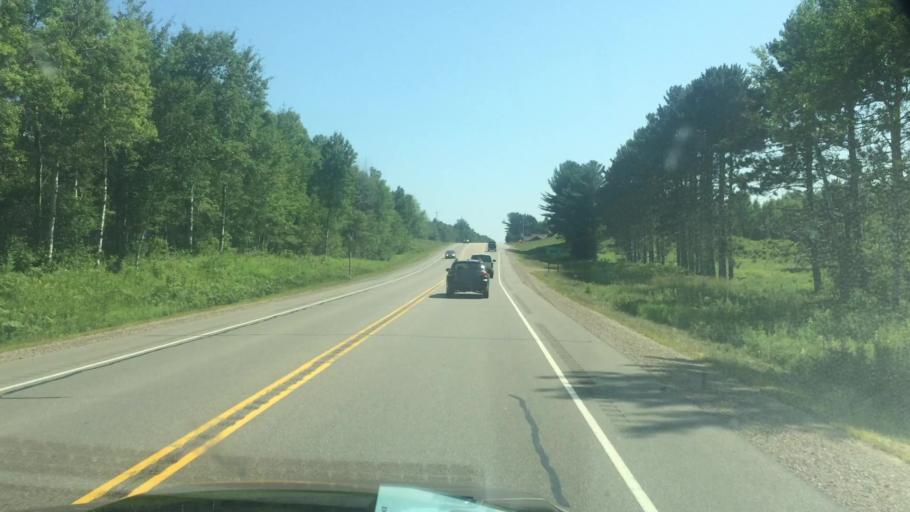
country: US
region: Wisconsin
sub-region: Oneida County
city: Rhinelander
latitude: 45.6114
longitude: -89.5444
